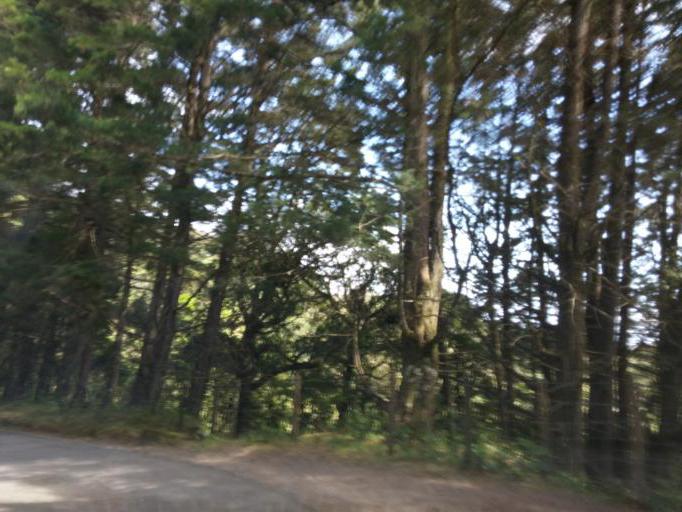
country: CR
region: Heredia
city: Santo Domingo
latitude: 10.0970
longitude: -84.1183
